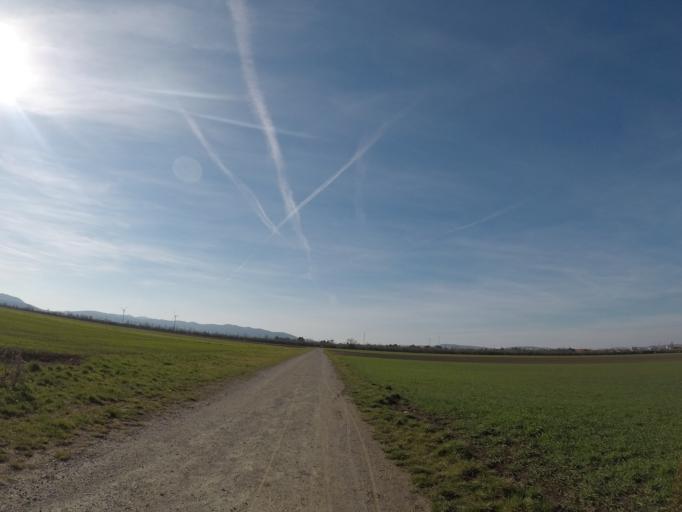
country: AT
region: Lower Austria
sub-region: Politischer Bezirk Modling
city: Vosendorf
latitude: 48.1124
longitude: 16.3449
